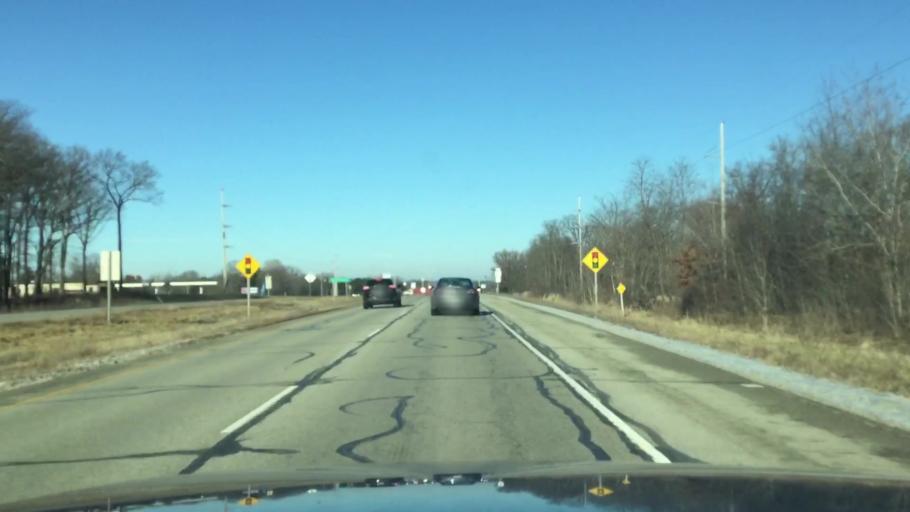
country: US
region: Wisconsin
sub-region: Racine County
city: Rochester
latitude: 42.7386
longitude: -88.2167
